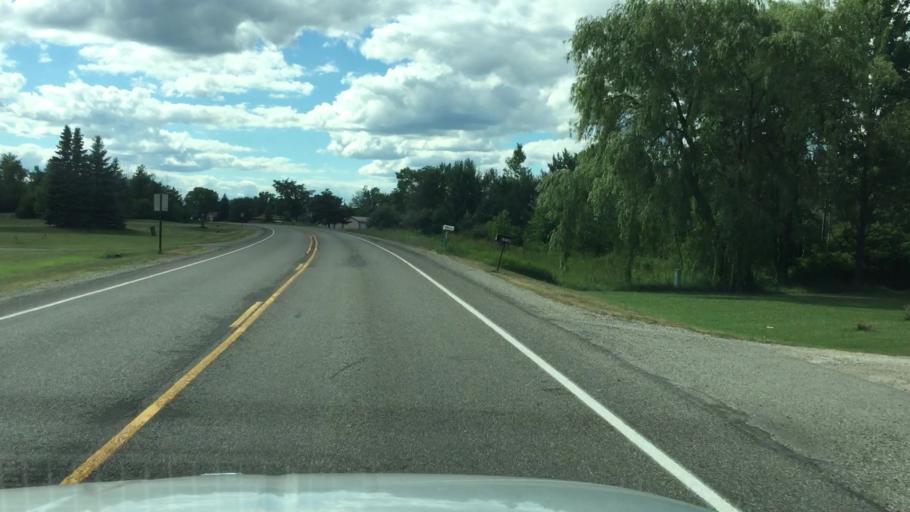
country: US
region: Michigan
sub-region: Saint Clair County
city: Capac
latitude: 43.0252
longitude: -82.9325
